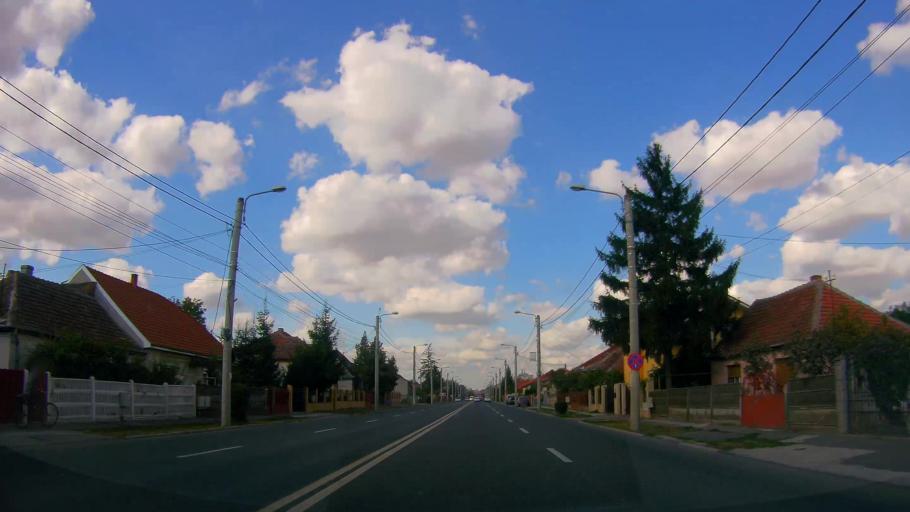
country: RO
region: Satu Mare
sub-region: Municipiul Satu Mare
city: Satu Mare
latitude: 47.7639
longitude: 22.8835
